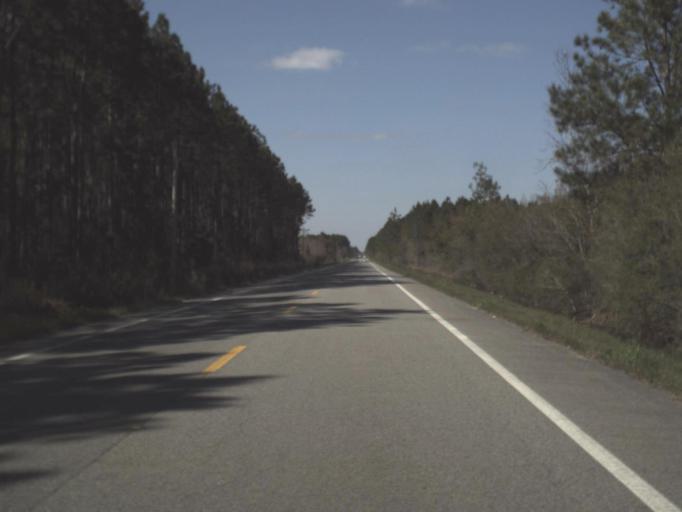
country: US
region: Florida
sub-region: Gulf County
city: Wewahitchka
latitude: 30.0176
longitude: -85.1776
